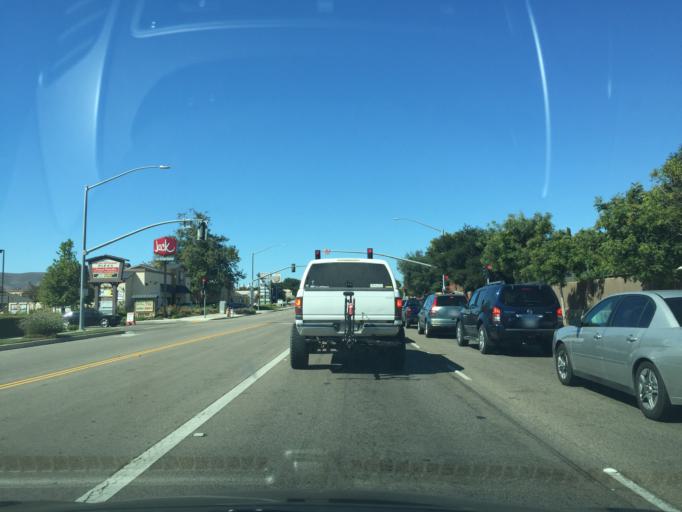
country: US
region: California
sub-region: Santa Barbara County
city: Buellton
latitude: 34.6103
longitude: -120.1853
